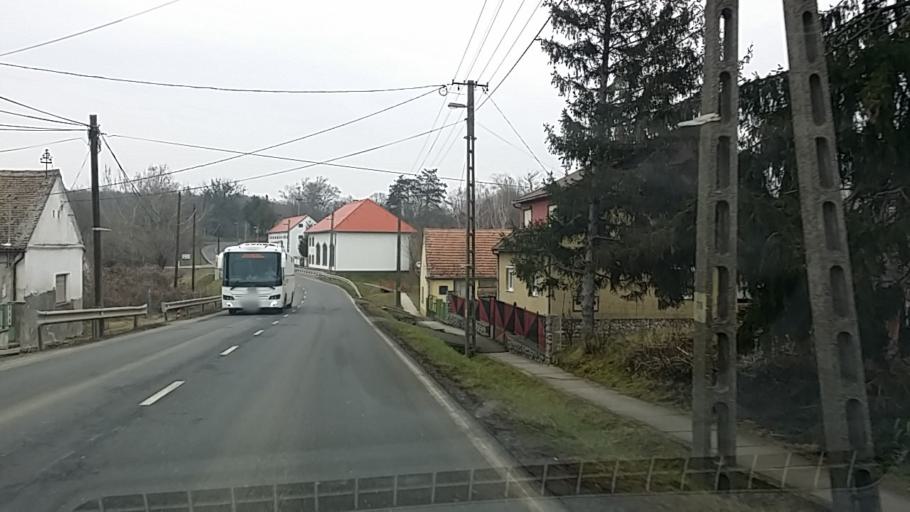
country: HU
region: Baranya
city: Dunaszekcso
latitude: 46.0532
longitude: 18.7187
